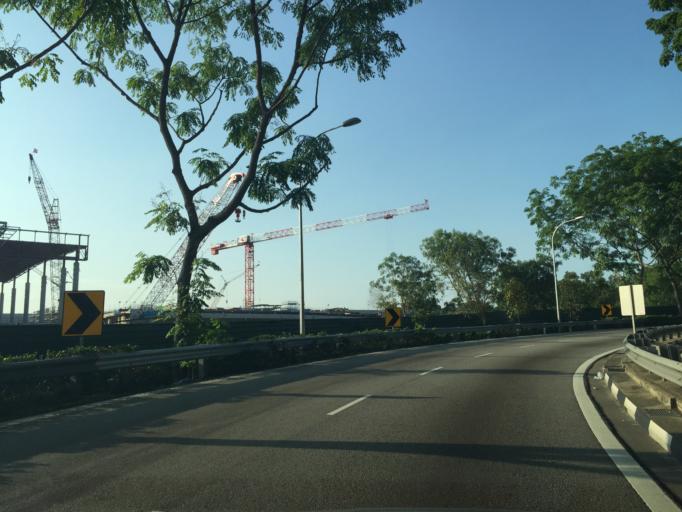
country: SG
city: Singapore
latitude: 1.3378
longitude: 103.9814
